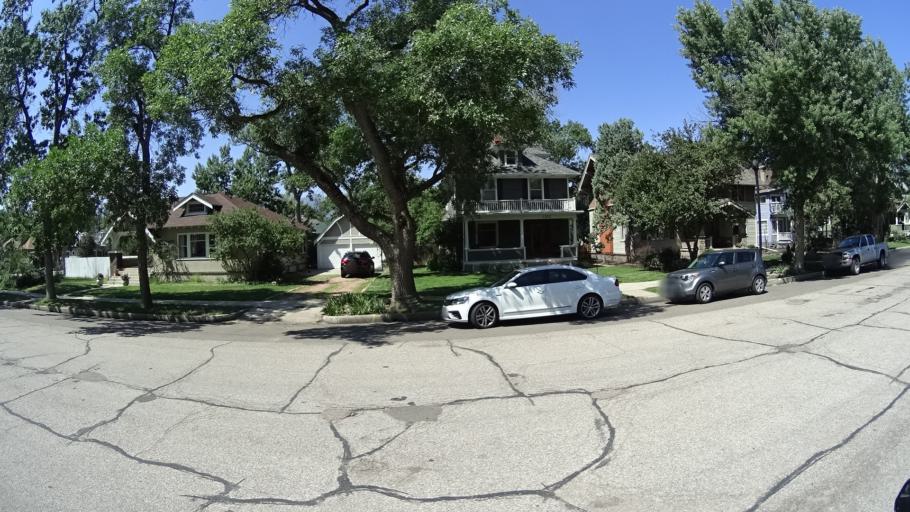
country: US
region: Colorado
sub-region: El Paso County
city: Colorado Springs
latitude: 38.8524
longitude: -104.8225
